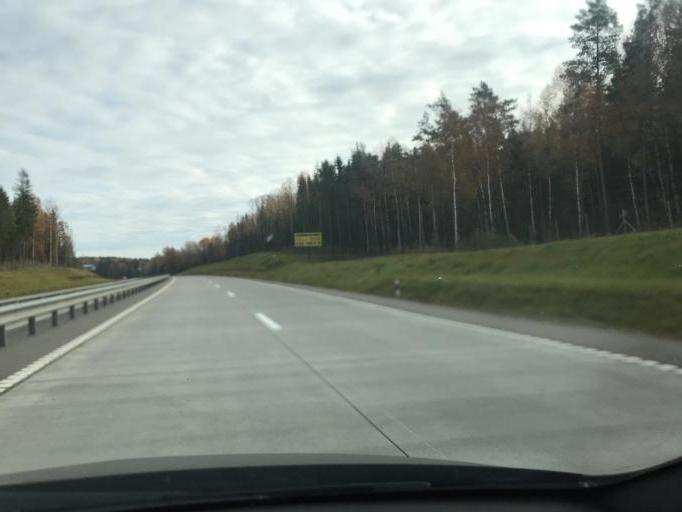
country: BY
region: Minsk
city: Syomkava
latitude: 54.0619
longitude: 27.4076
